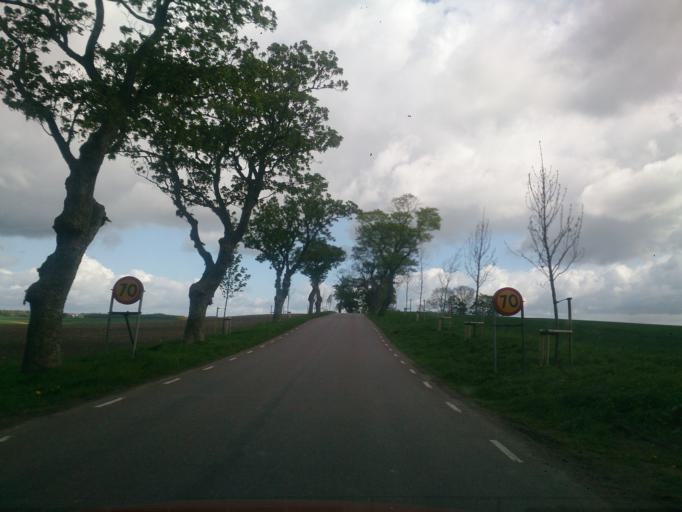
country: SE
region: Skane
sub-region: Ystads Kommun
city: Ystad
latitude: 55.4644
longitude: 13.7058
